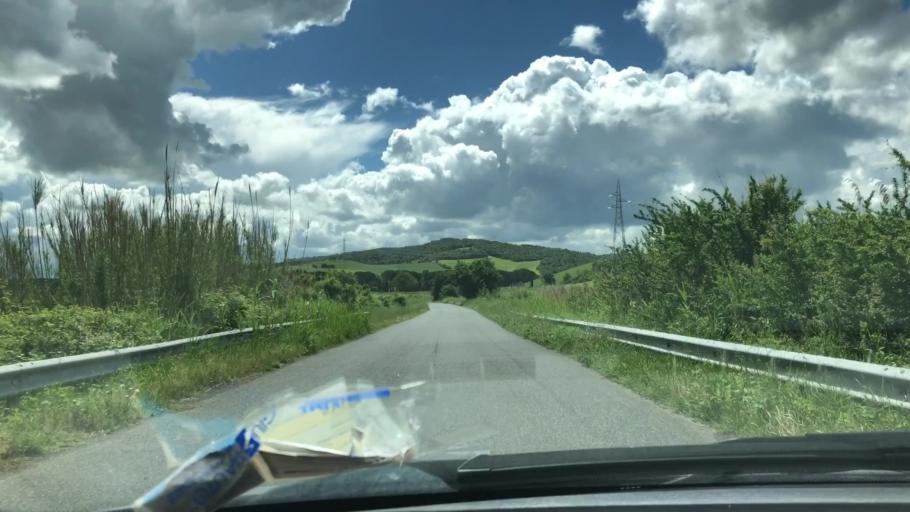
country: IT
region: Tuscany
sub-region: Province of Pisa
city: Saline
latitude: 43.3525
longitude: 10.7875
